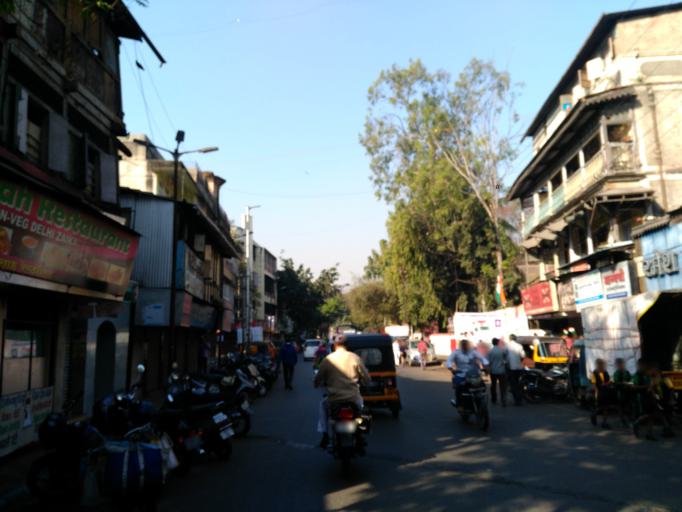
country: IN
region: Maharashtra
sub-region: Pune Division
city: Pune
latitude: 18.5165
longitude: 73.8729
